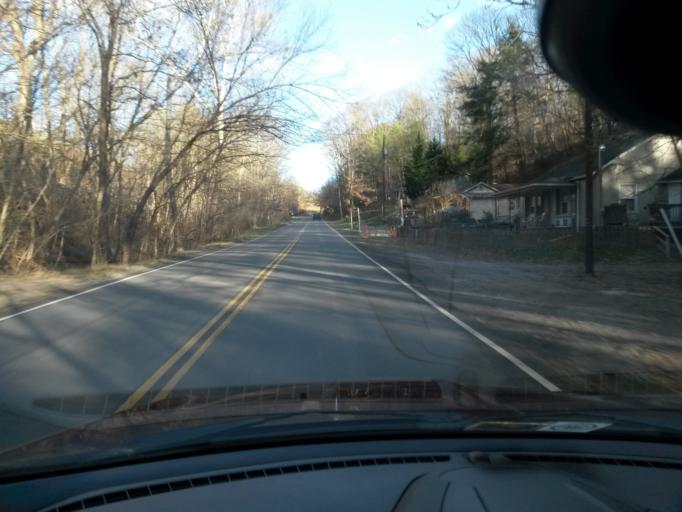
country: US
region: Virginia
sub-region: Giles County
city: Narrows
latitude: 37.3878
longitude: -80.8158
